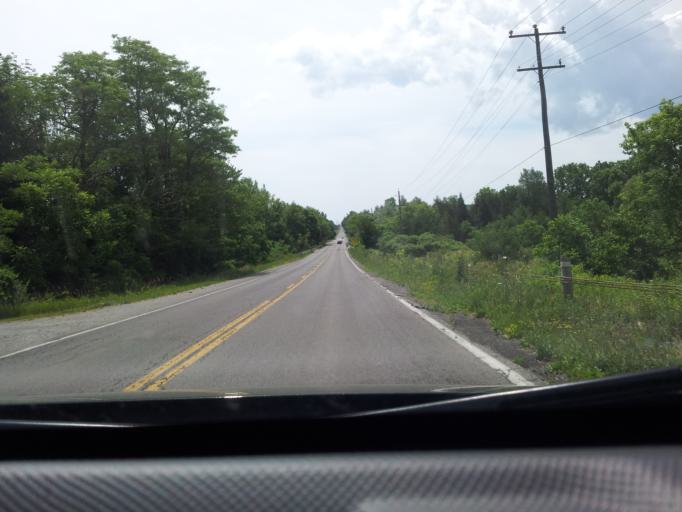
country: CA
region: Ontario
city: Norfolk County
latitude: 42.8107
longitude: -80.2481
